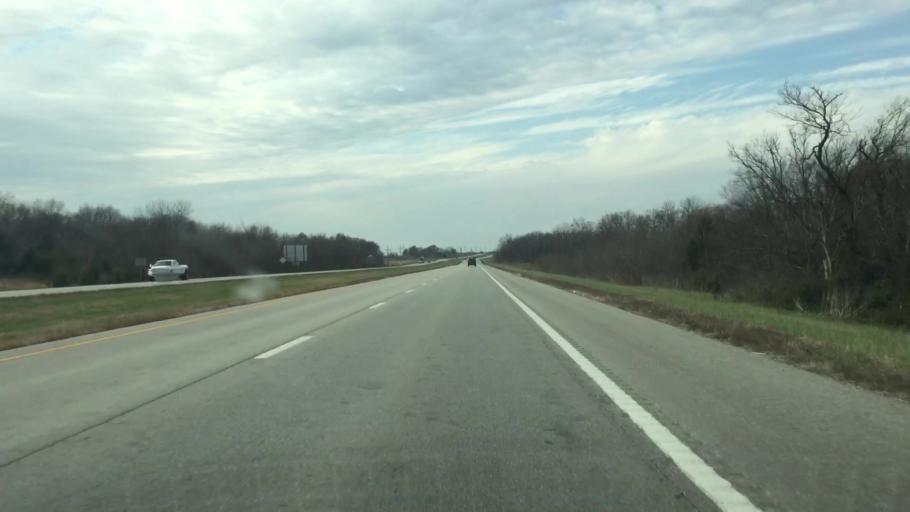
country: US
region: Missouri
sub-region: Cass County
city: Garden City
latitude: 38.5794
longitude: -94.2124
